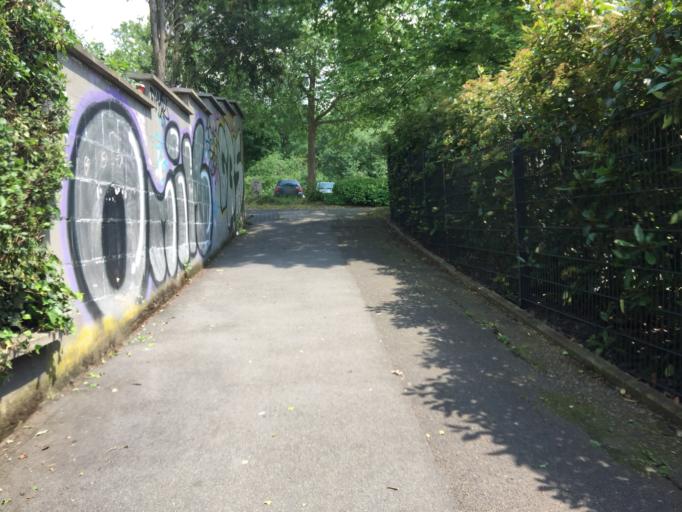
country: DE
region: Hesse
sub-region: Regierungsbezirk Darmstadt
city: Wiesbaden
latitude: 50.0787
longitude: 8.2580
